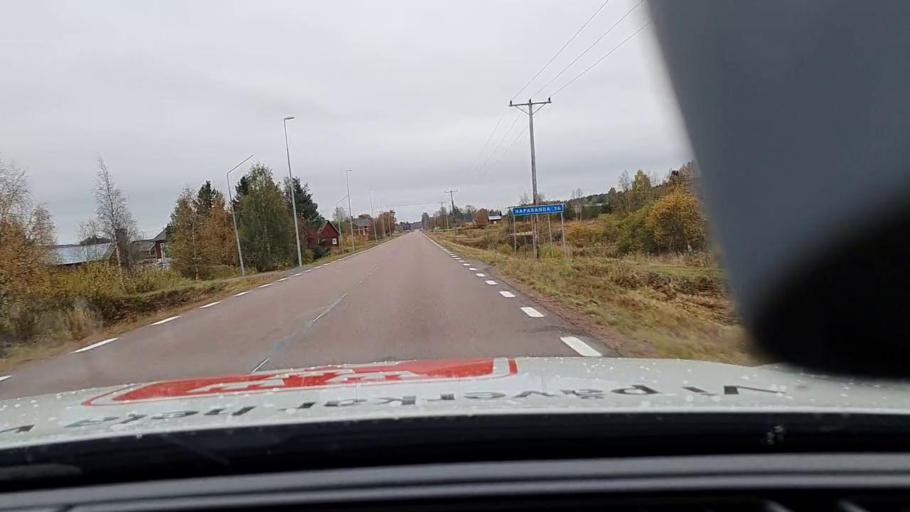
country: FI
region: Lapland
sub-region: Torniolaakso
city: Ylitornio
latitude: 66.1385
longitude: 23.9015
